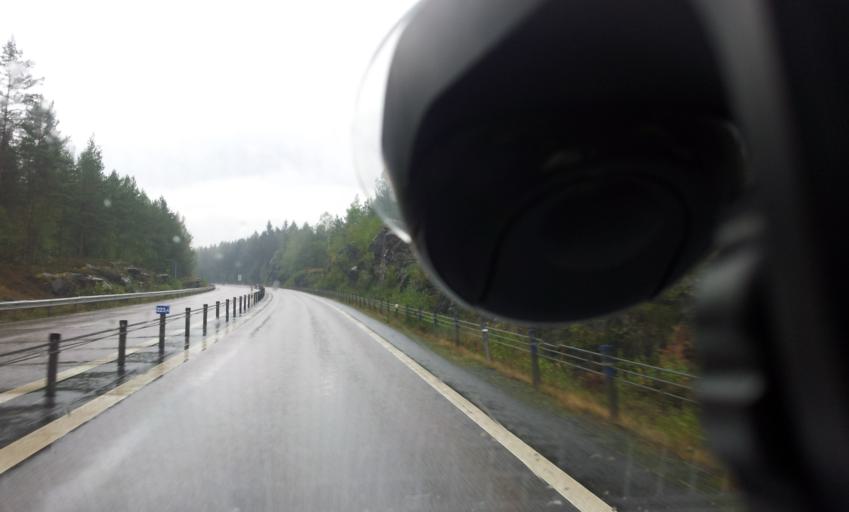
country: SE
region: Kalmar
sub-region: Vasterviks Kommun
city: Forserum
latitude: 58.0334
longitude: 16.5152
